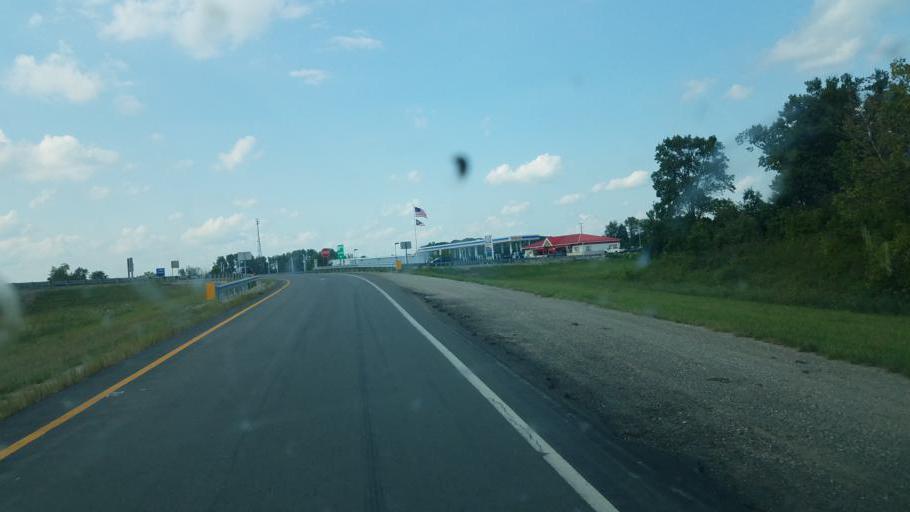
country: US
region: Ohio
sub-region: Knox County
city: Fredericktown
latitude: 40.4776
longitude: -82.5564
